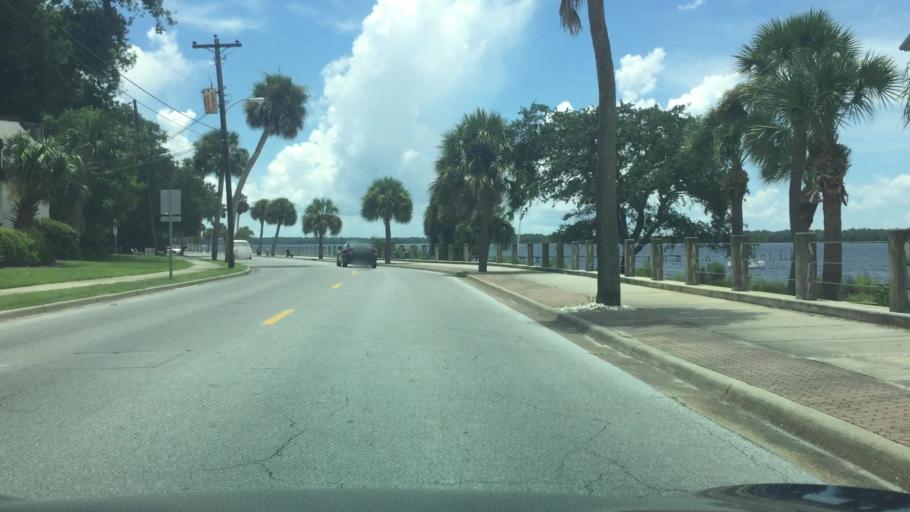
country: US
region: Florida
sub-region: Bay County
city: Panama City
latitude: 30.1493
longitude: -85.6590
